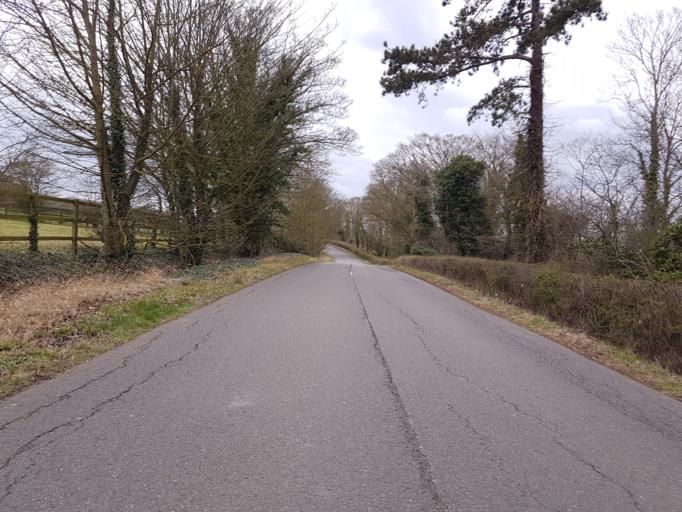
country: GB
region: England
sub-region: Cambridgeshire
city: Girton
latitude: 52.2170
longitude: 0.0610
